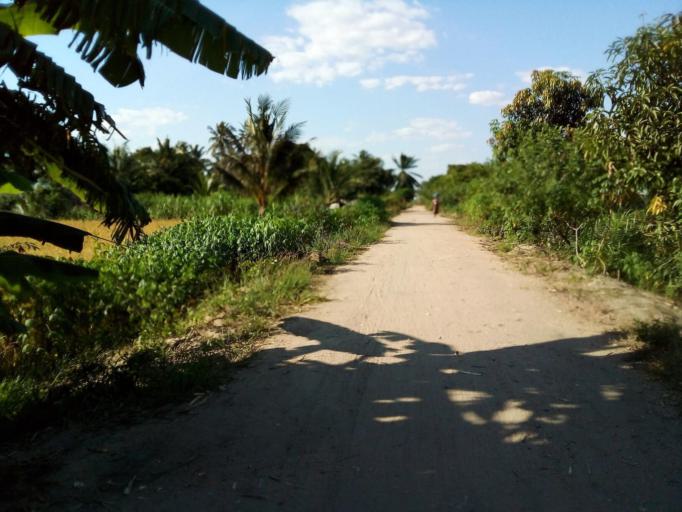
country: MZ
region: Zambezia
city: Quelimane
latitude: -17.5939
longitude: 36.8318
